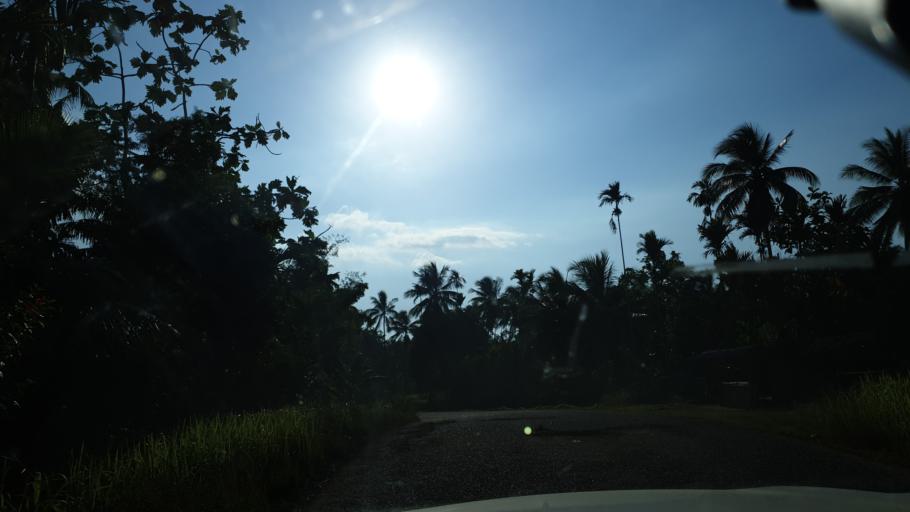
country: PG
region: East Sepik
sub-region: Wewak
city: Wewak
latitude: -3.6966
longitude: 143.6455
